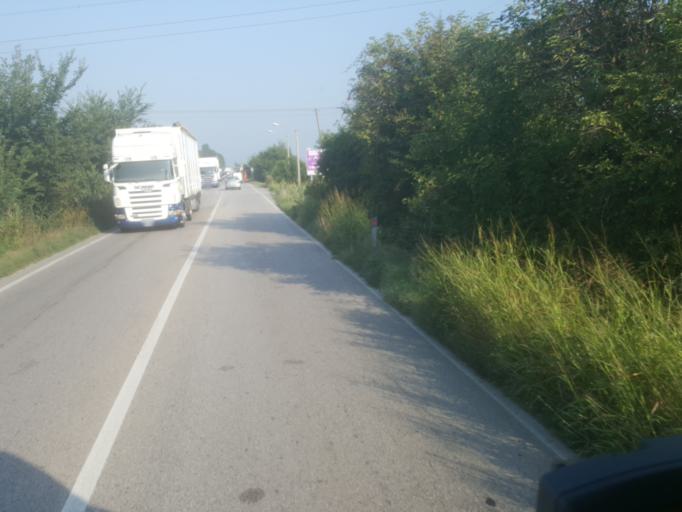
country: IT
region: Emilia-Romagna
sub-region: Provincia di Ravenna
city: Fornace Zarattini
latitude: 44.4308
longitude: 12.1510
